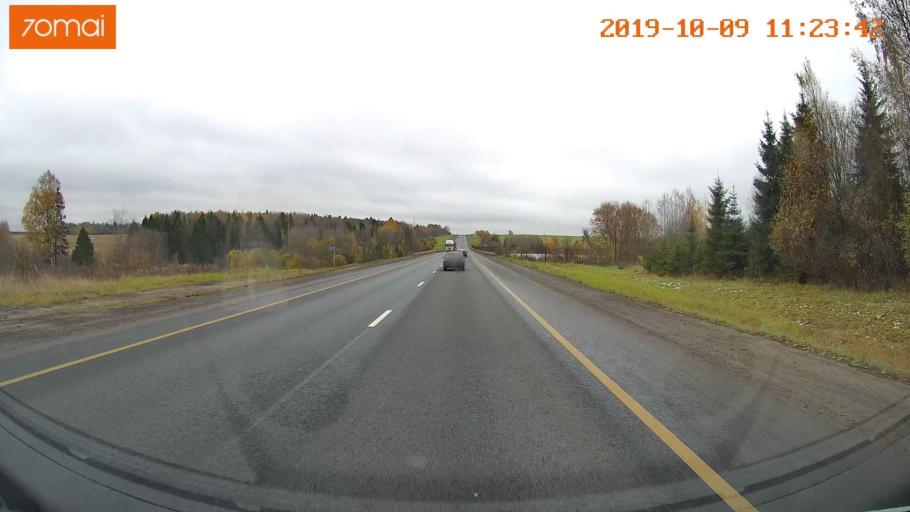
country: RU
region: Vologda
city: Vologda
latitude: 59.1183
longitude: 39.9726
